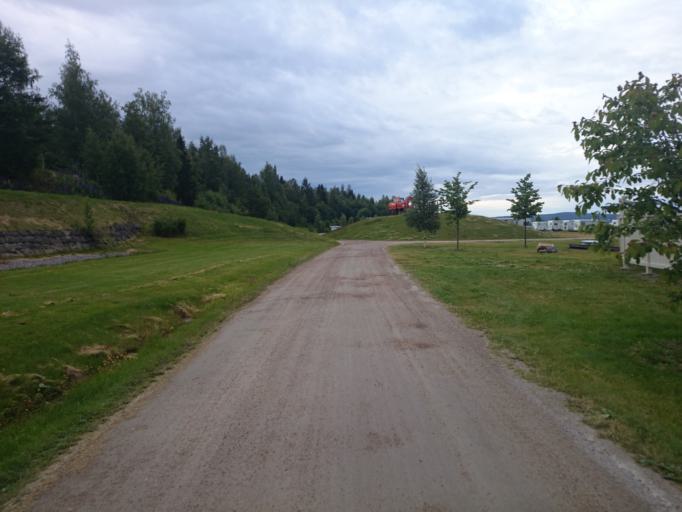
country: SE
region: Vaesternorrland
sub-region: Sundsvalls Kommun
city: Stockvik
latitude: 62.3200
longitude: 17.3696
